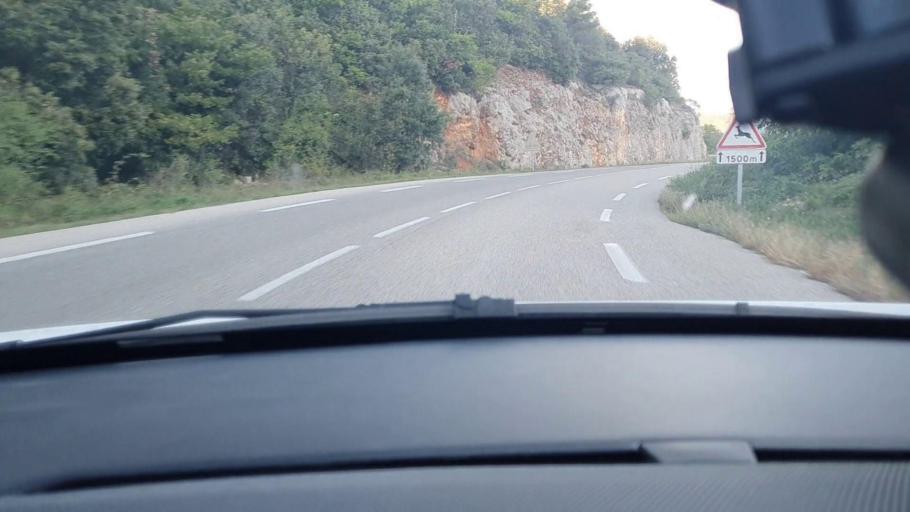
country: FR
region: Languedoc-Roussillon
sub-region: Departement du Gard
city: Barjac
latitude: 44.2306
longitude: 4.3069
